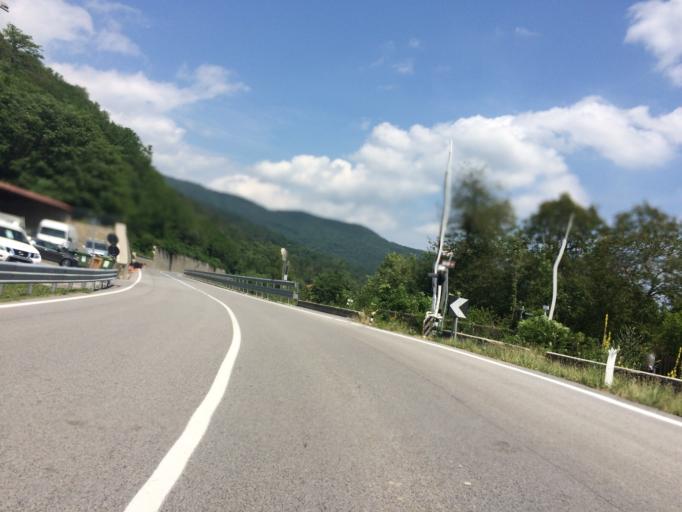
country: IT
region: Piedmont
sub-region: Provincia di Cuneo
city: Priola
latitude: 44.2511
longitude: 8.0215
